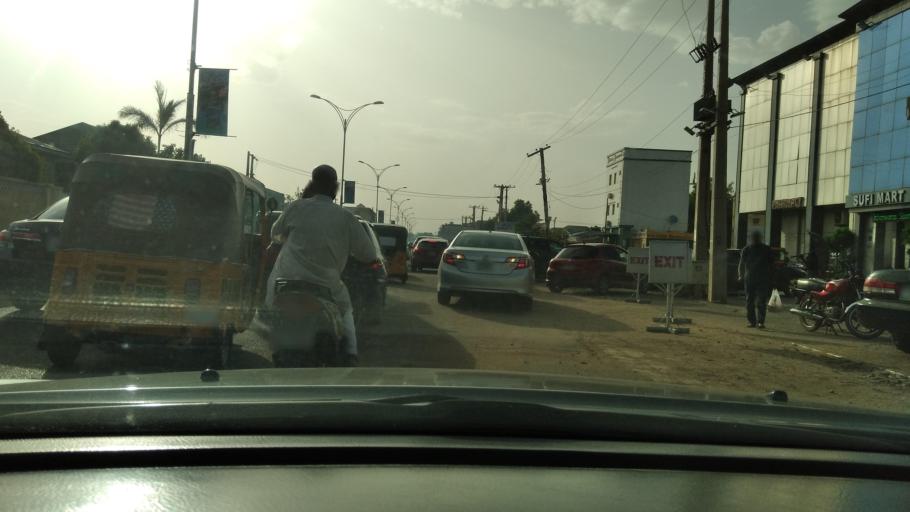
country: NG
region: Kano
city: Kano
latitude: 11.9779
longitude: 8.5643
